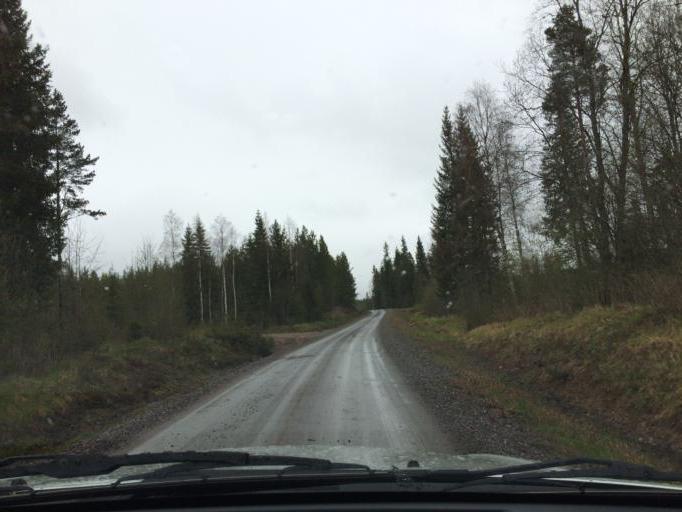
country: SE
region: Dalarna
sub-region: Ludvika Kommun
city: Abborrberget
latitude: 60.0271
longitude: 14.6378
